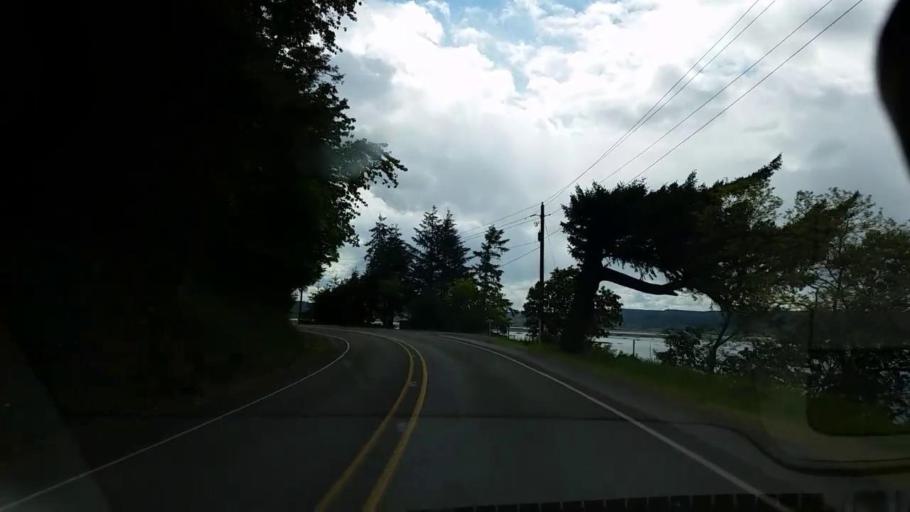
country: US
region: Washington
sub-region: Mason County
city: Shelton
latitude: 47.3568
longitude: -123.1052
